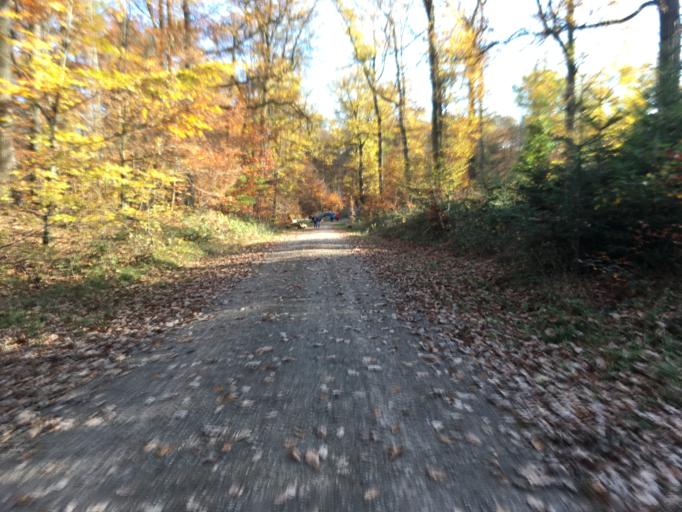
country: DE
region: Baden-Wuerttemberg
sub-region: Karlsruhe Region
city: Sternenfels
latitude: 49.0435
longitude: 8.8227
